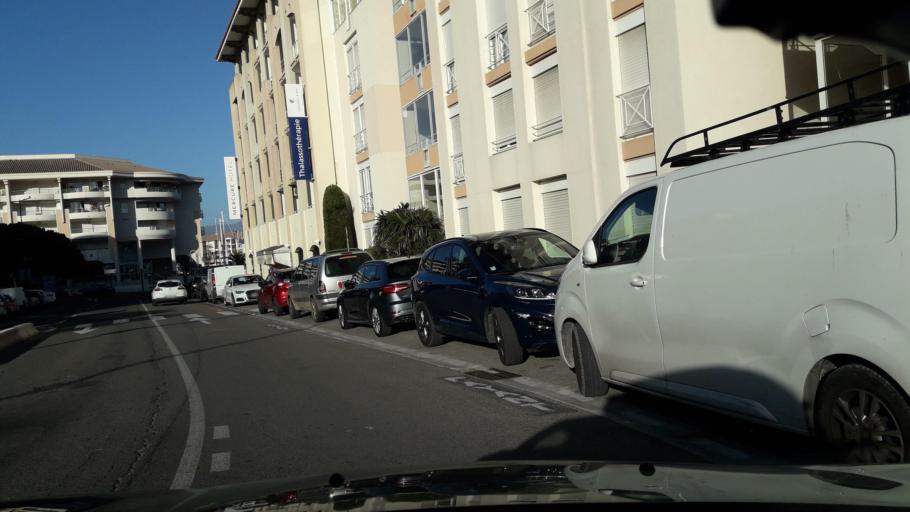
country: FR
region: Provence-Alpes-Cote d'Azur
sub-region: Departement du Var
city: Frejus
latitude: 43.4197
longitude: 6.7460
